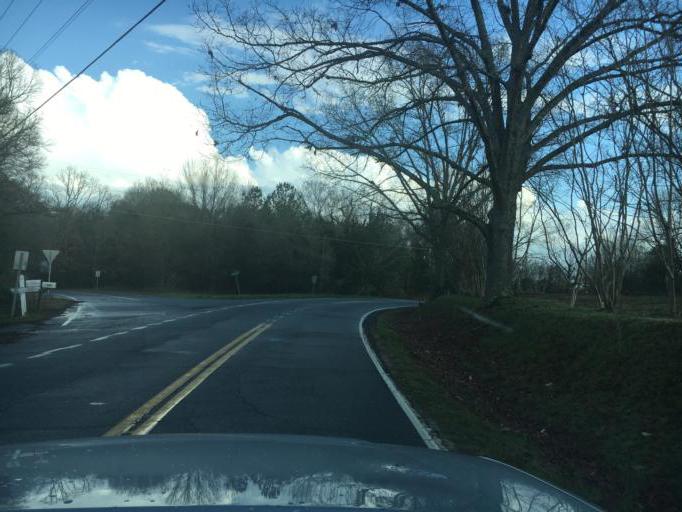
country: US
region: South Carolina
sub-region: Greenville County
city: Parker
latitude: 34.8539
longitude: -82.4966
